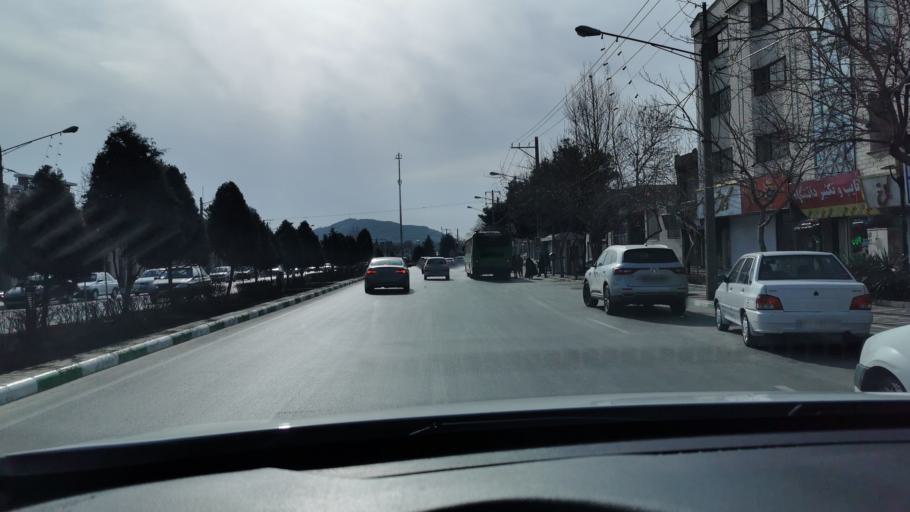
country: IR
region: Razavi Khorasan
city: Mashhad
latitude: 36.2851
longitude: 59.5475
